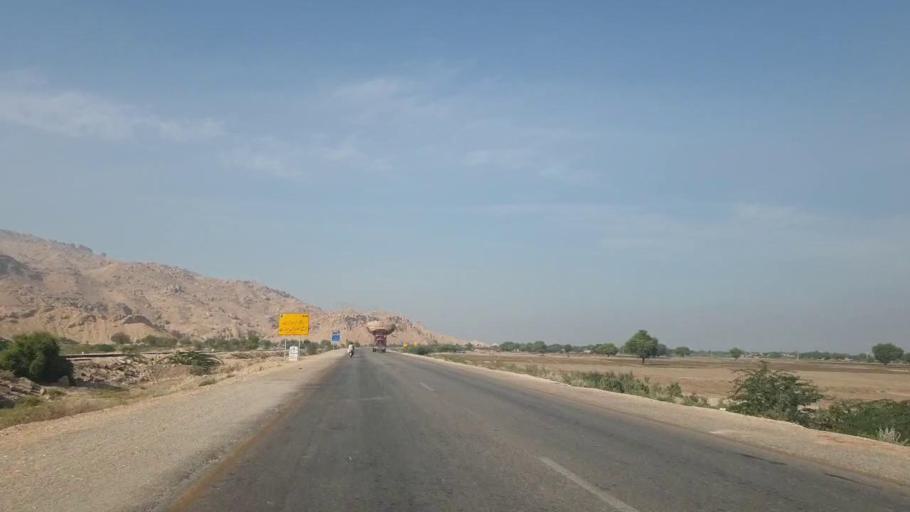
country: PK
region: Sindh
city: Sehwan
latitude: 26.2839
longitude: 67.8953
